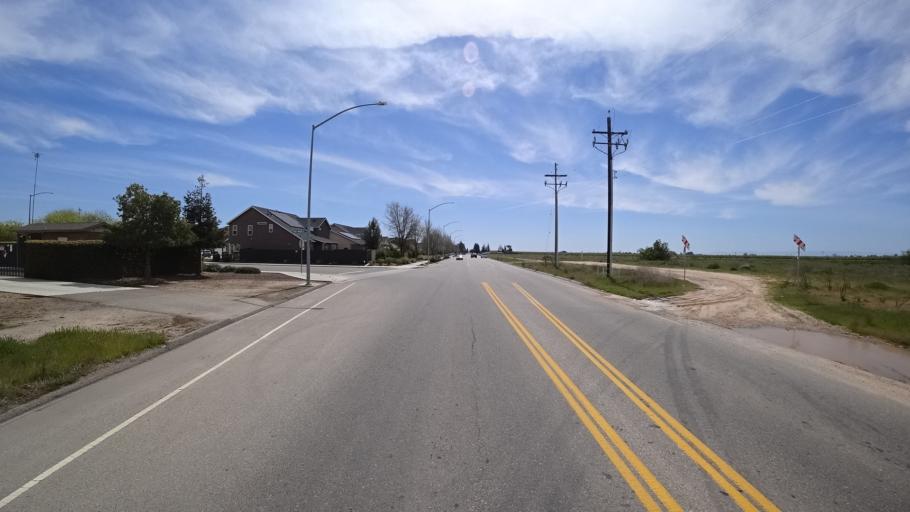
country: US
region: California
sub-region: Fresno County
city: Biola
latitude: 36.8147
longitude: -119.9256
